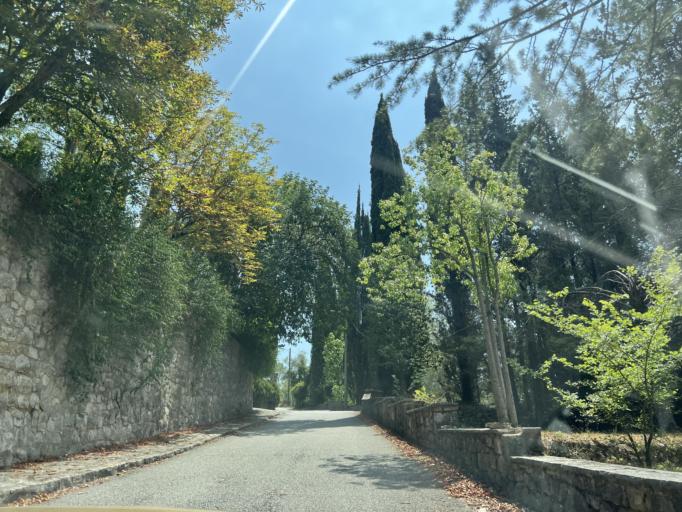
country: FR
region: Provence-Alpes-Cote d'Azur
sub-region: Departement des Alpes-Maritimes
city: Le Rouret
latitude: 43.7026
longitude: 7.0048
